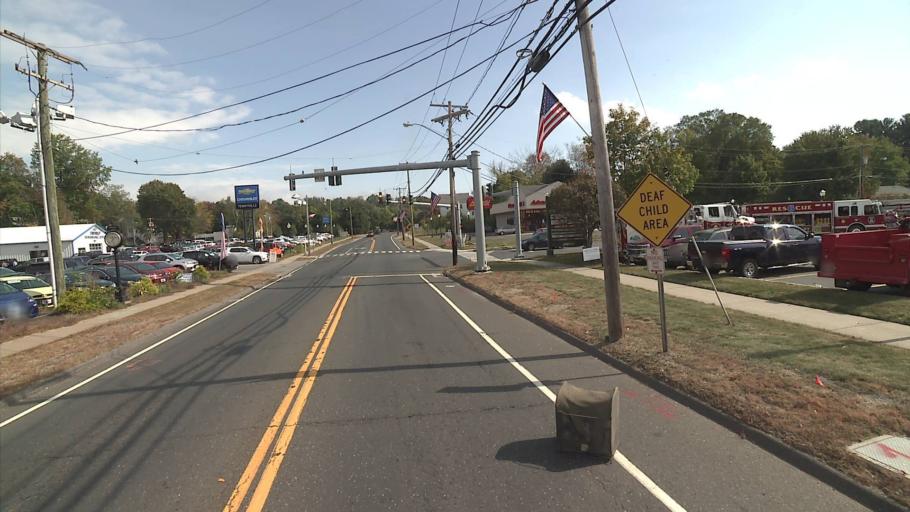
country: US
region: Connecticut
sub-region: Litchfield County
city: Terryville
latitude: 41.6799
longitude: -73.0193
